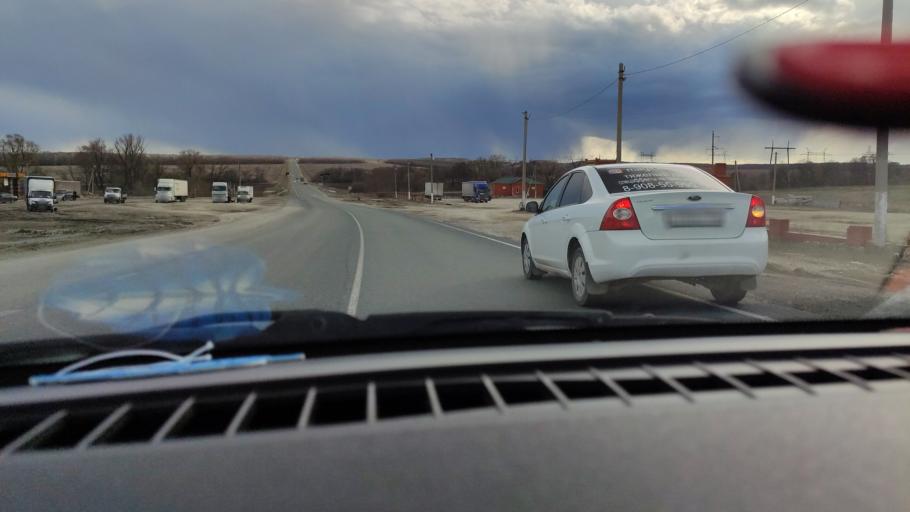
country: RU
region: Saratov
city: Sinodskoye
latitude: 51.9204
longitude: 46.5611
